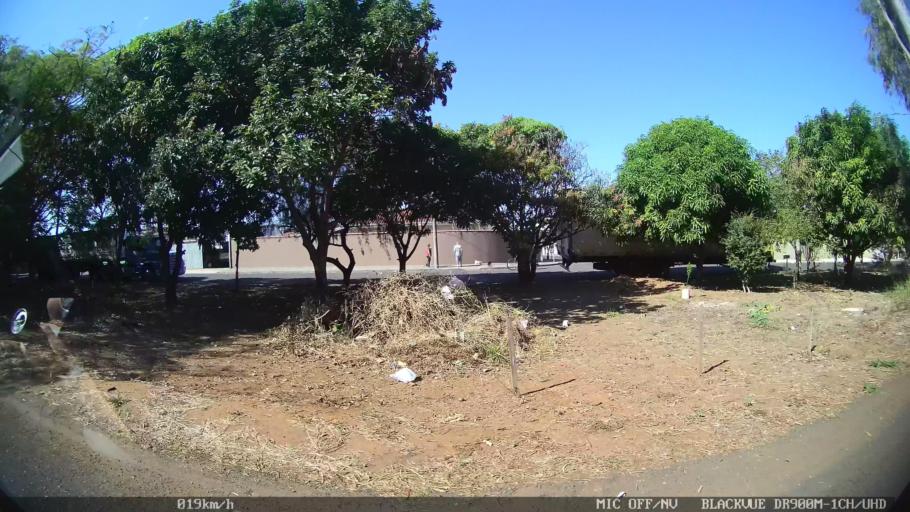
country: BR
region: Sao Paulo
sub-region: Batatais
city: Batatais
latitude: -20.8765
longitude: -47.5953
